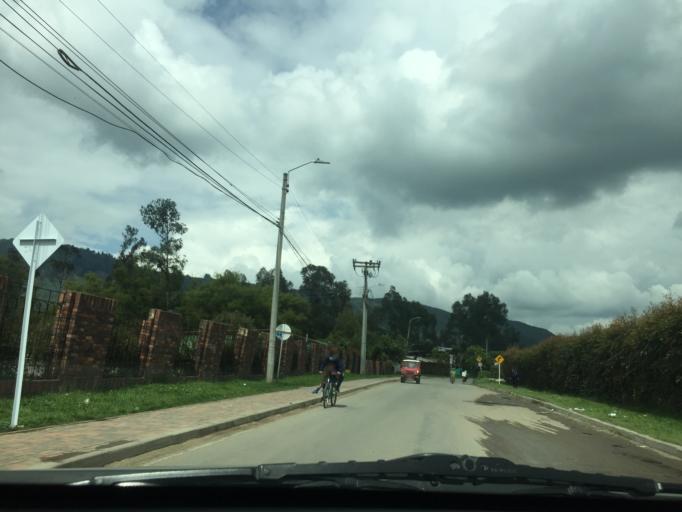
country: CO
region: Cundinamarca
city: Chia
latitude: 4.8707
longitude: -74.0631
